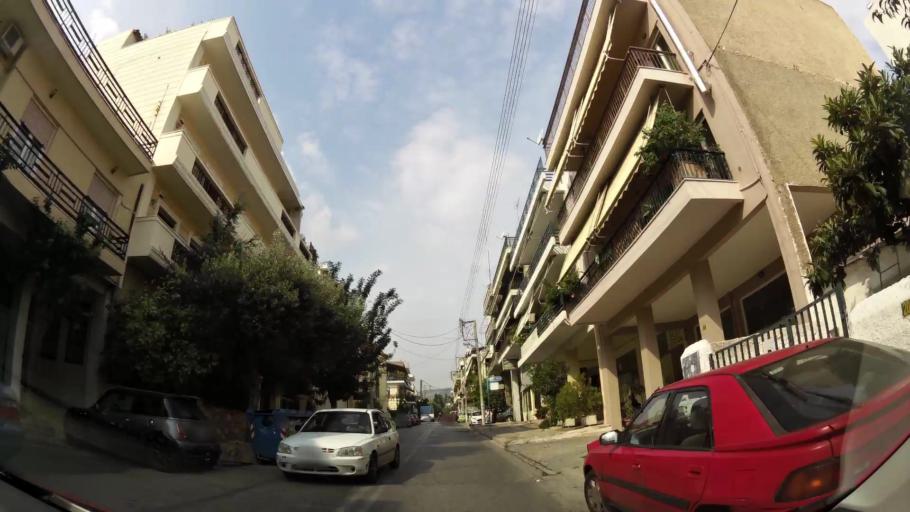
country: GR
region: Attica
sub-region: Nomarchia Athinas
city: Chaidari
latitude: 38.0178
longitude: 23.6724
